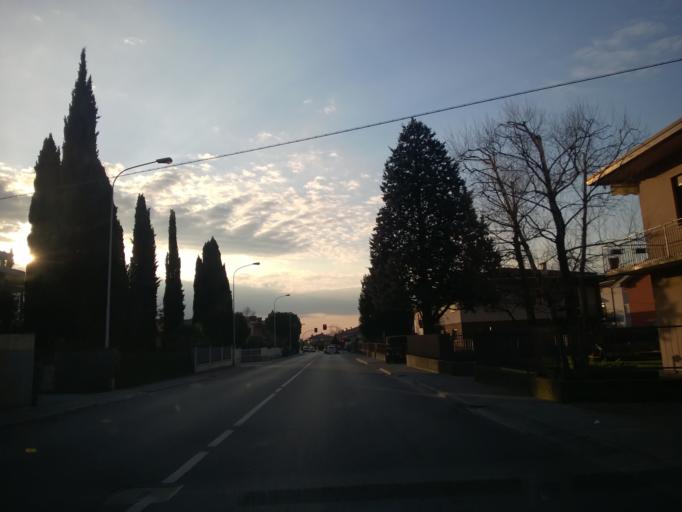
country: IT
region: Veneto
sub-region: Provincia di Vicenza
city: Zane
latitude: 45.7216
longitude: 11.4605
